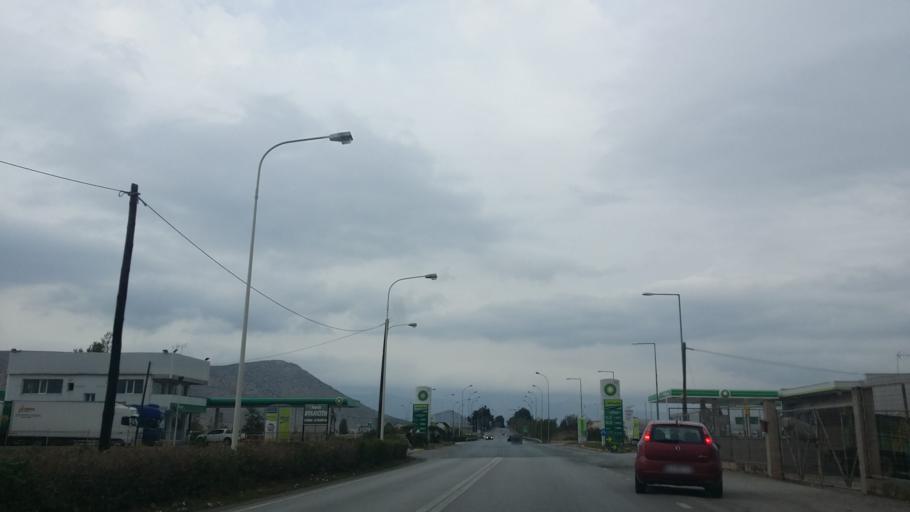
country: GR
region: Central Greece
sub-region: Nomos Voiotias
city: Thivai
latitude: 38.3591
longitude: 23.3222
